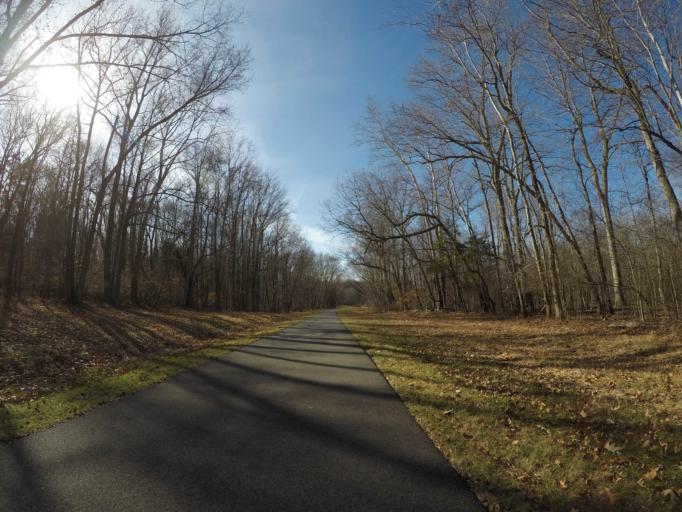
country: US
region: Maryland
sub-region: Charles County
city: Bennsville
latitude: 38.5956
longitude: -77.0123
